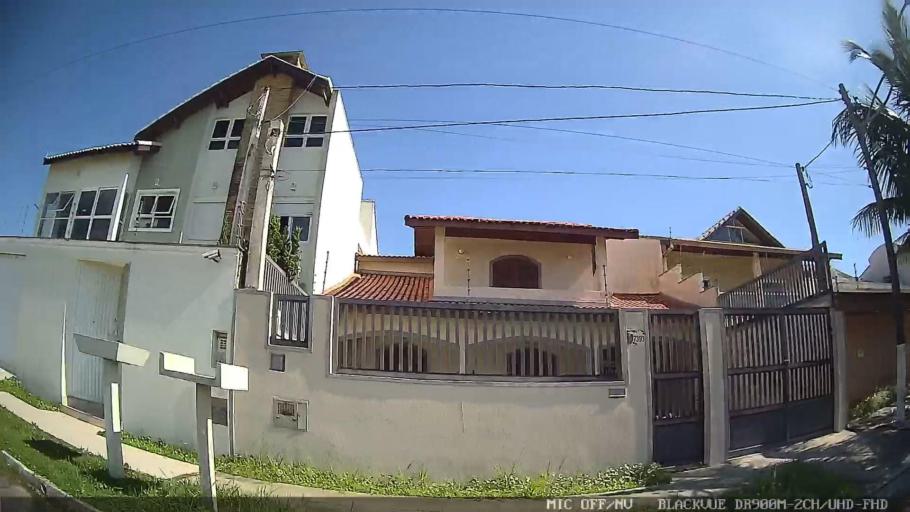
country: BR
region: Sao Paulo
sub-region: Peruibe
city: Peruibe
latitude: -24.2850
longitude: -46.9488
